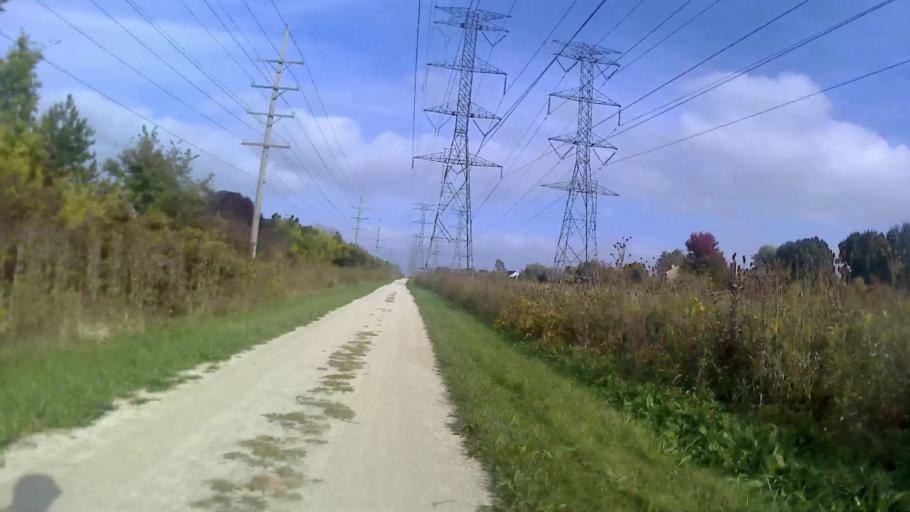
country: US
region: Illinois
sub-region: Kane County
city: Aurora
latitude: 41.7922
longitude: -88.2592
